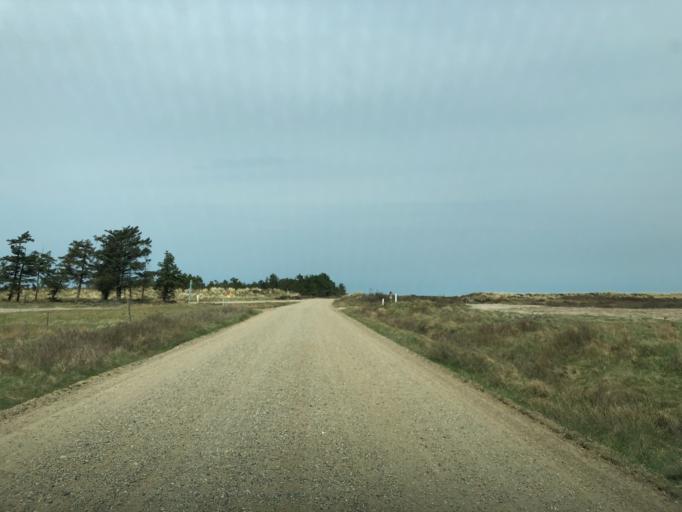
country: DK
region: South Denmark
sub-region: Varde Kommune
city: Oksbol
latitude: 55.5661
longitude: 8.1353
